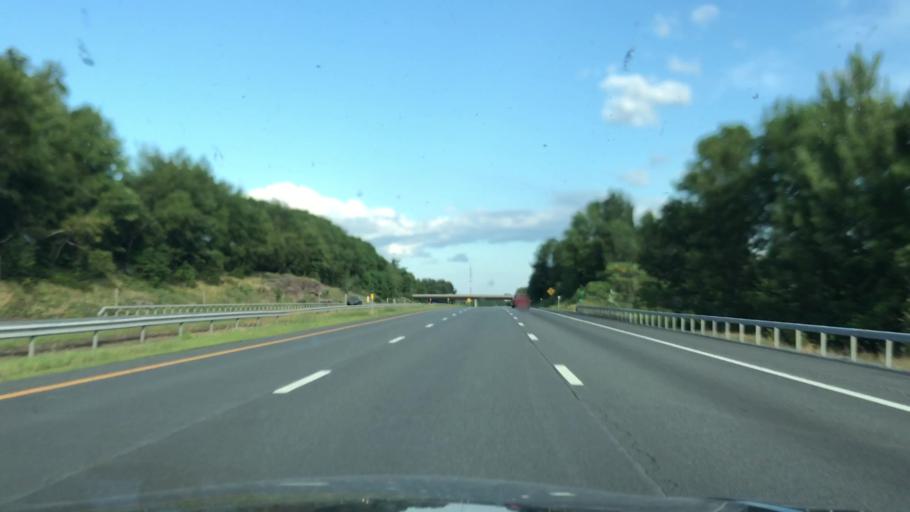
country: US
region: New York
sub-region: Sullivan County
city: Monticello
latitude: 41.6681
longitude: -74.7056
